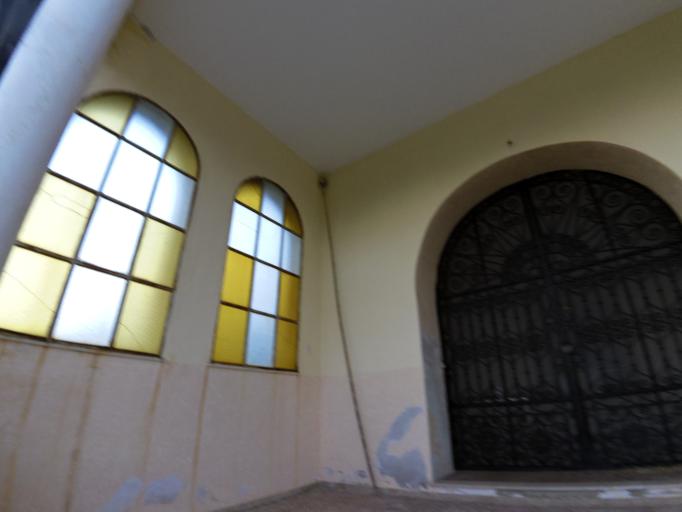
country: IT
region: Calabria
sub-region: Provincia di Reggio Calabria
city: Caulonia
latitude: 38.3877
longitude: 16.3986
